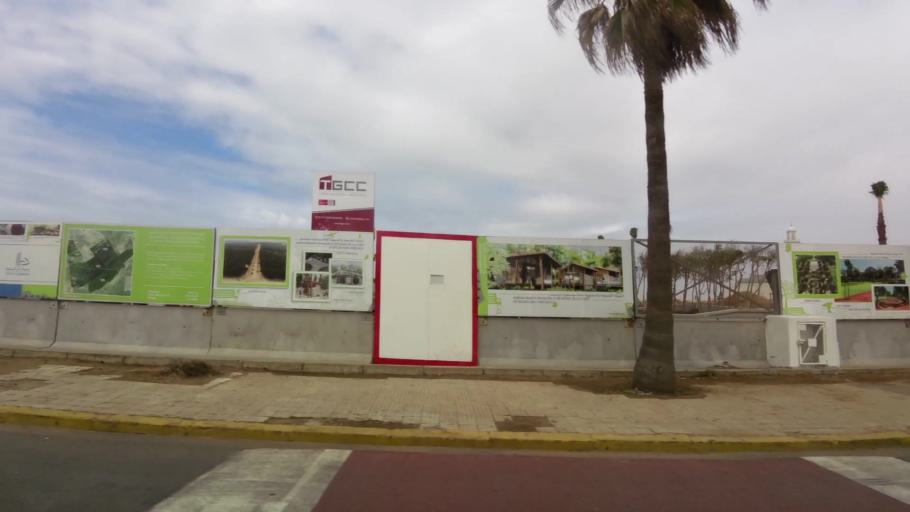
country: MA
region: Grand Casablanca
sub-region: Casablanca
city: Casablanca
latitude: 33.6047
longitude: -7.6465
